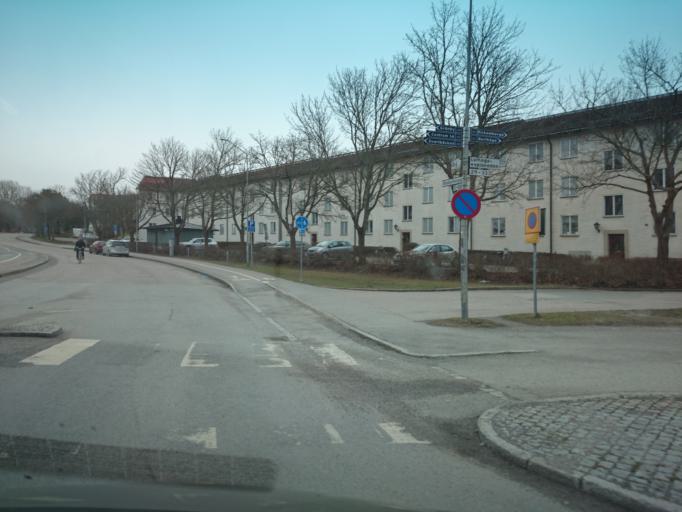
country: SE
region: Uppsala
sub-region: Uppsala Kommun
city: Uppsala
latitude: 59.8589
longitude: 17.6152
